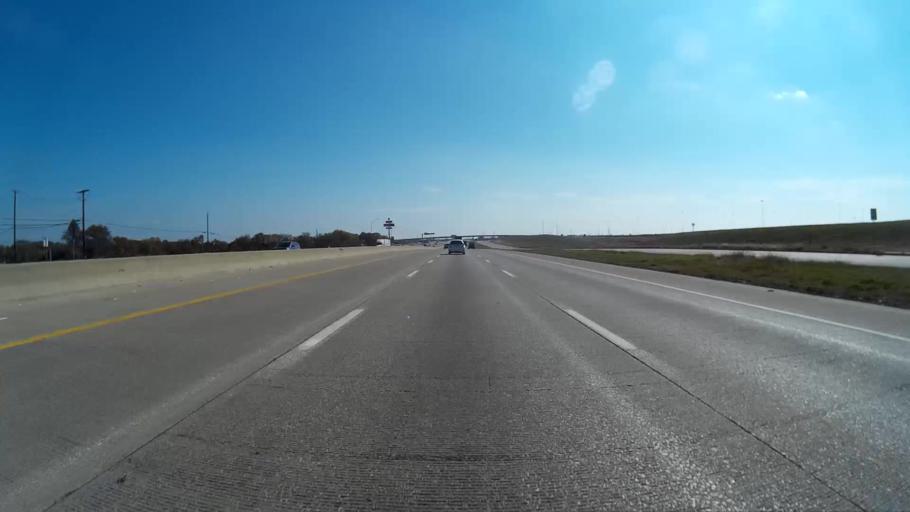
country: US
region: Texas
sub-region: Dallas County
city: Hutchins
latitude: 32.6277
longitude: -96.6971
